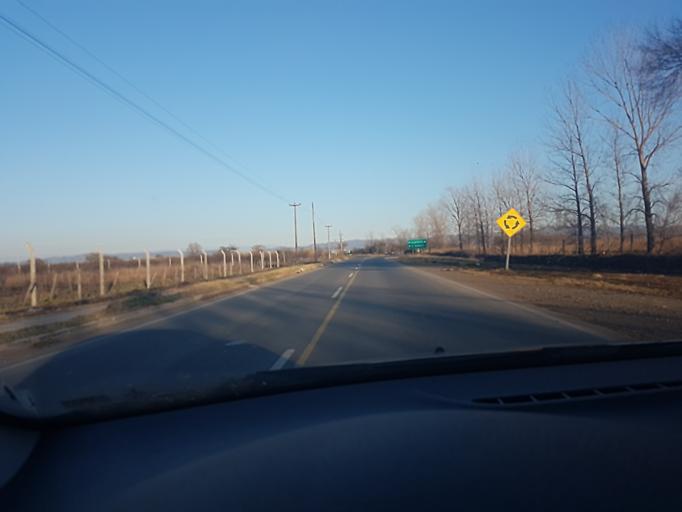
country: AR
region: Cordoba
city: Villa Allende
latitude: -31.3158
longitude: -64.2220
